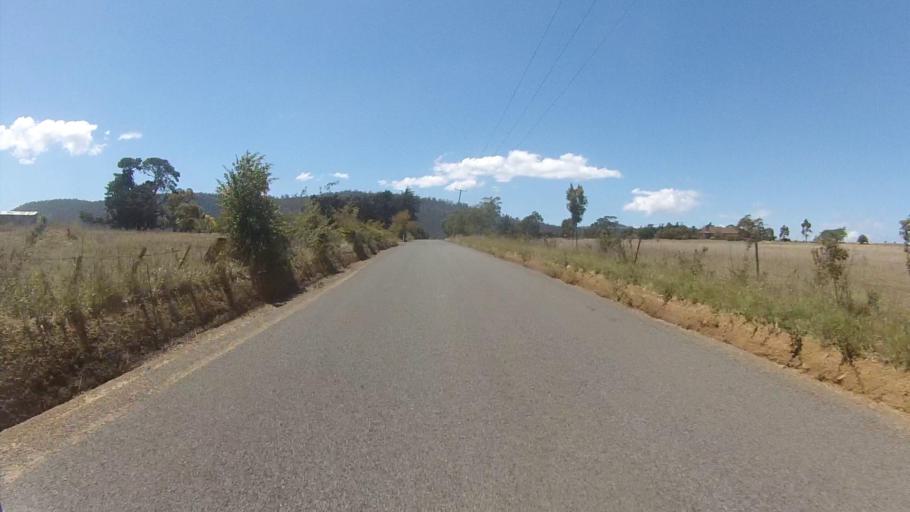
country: AU
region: Tasmania
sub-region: Sorell
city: Sorell
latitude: -42.7617
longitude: 147.6194
